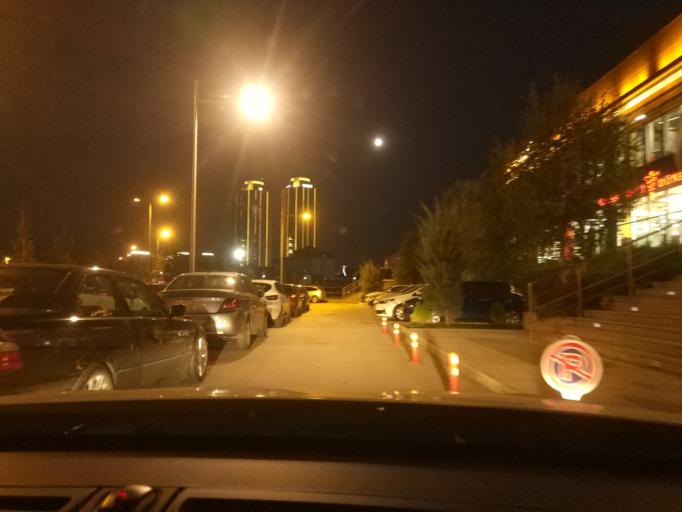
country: TR
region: Ankara
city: Batikent
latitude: 39.9101
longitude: 32.7550
